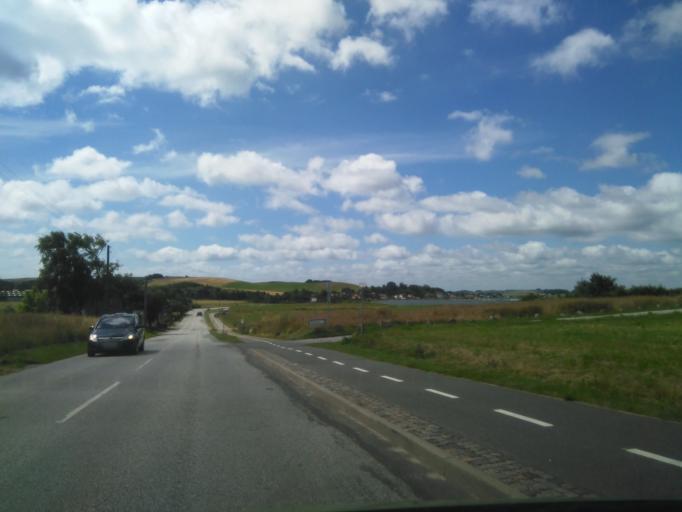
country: DK
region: Central Jutland
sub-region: Syddjurs Kommune
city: Ronde
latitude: 56.2106
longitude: 10.4850
